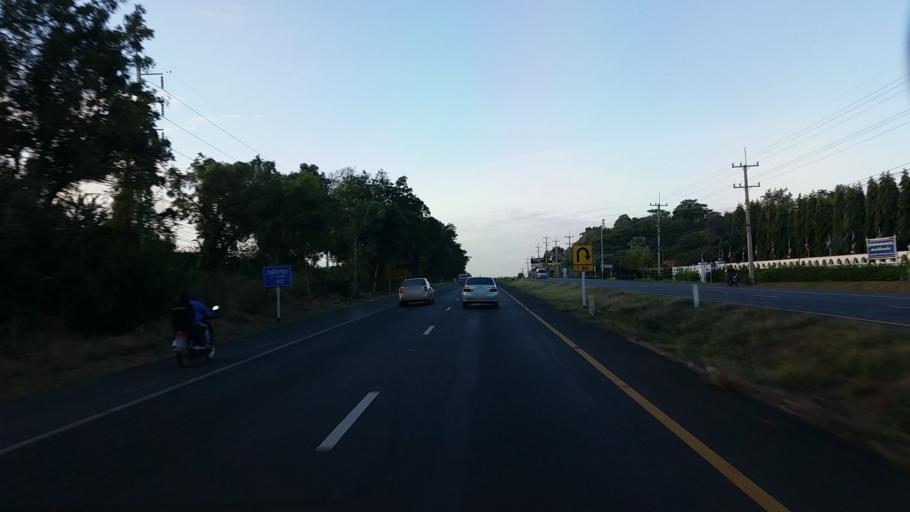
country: TH
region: Lop Buri
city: Chai Badan
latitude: 15.1575
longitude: 101.0573
